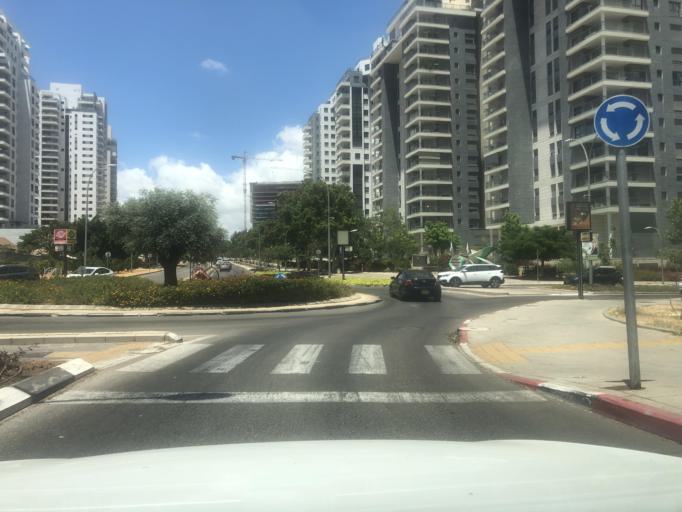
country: IL
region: Central District
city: Hod HaSharon
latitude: 32.1641
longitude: 34.9022
